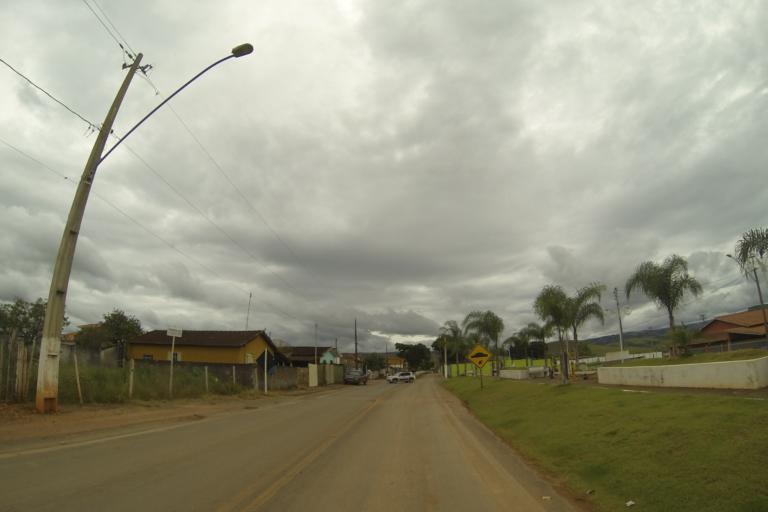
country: BR
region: Minas Gerais
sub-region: Bambui
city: Bambui
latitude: -19.9982
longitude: -46.2163
